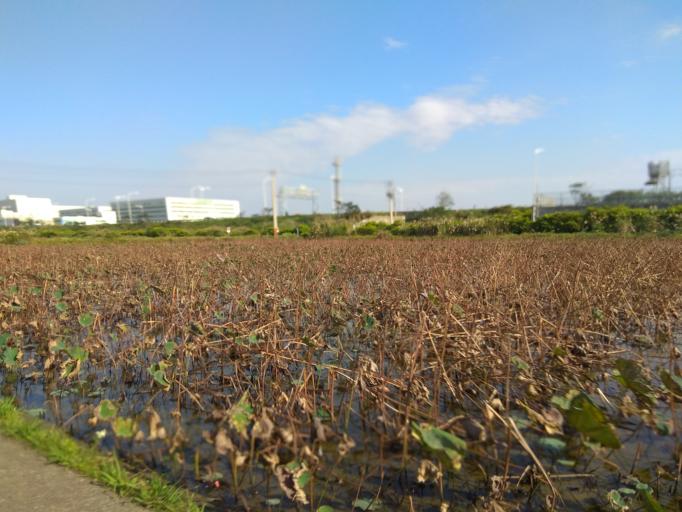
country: TW
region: Taiwan
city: Taoyuan City
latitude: 25.0638
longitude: 121.2132
